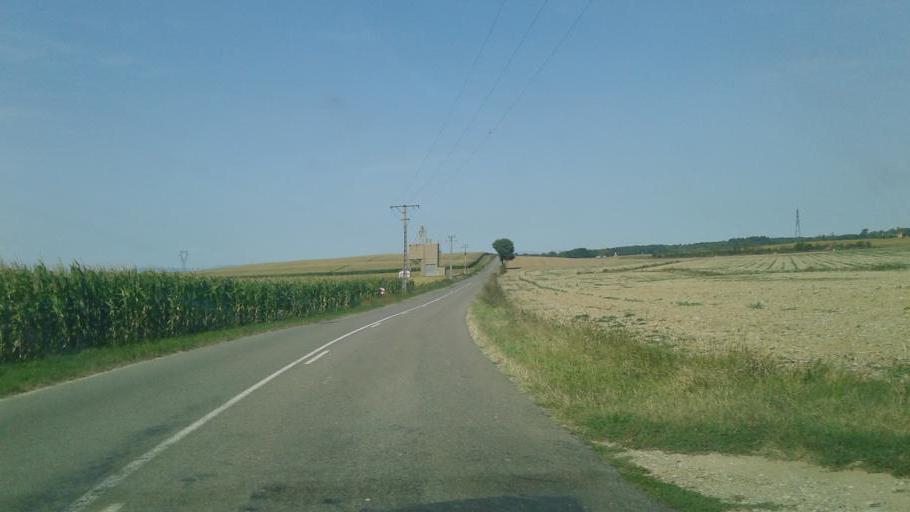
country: FR
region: Rhone-Alpes
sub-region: Departement de l'Ain
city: Beynost
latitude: 45.8589
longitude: 5.0104
